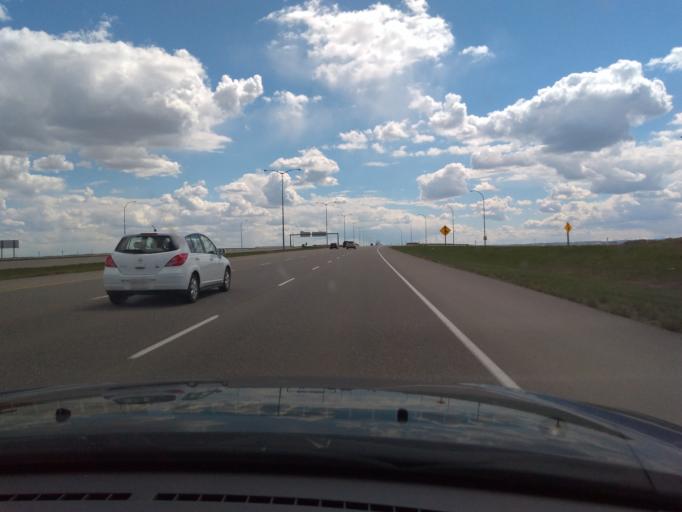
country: CA
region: Alberta
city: Chestermere
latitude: 50.9758
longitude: -113.9204
